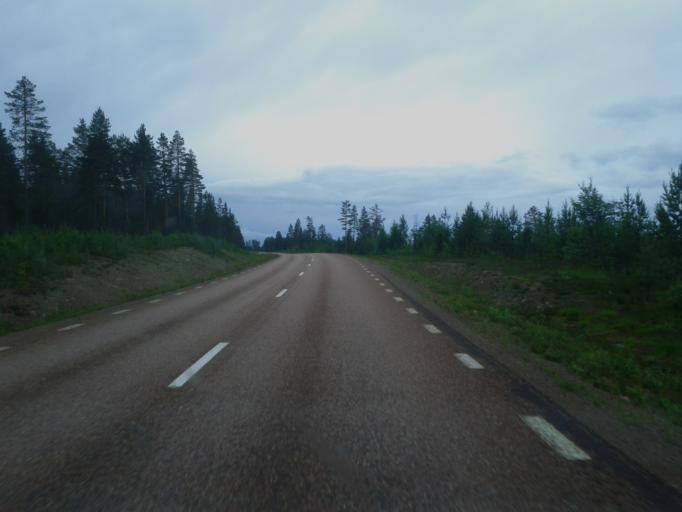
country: SE
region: Dalarna
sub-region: Alvdalens Kommun
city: AElvdalen
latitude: 61.4782
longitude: 13.4231
